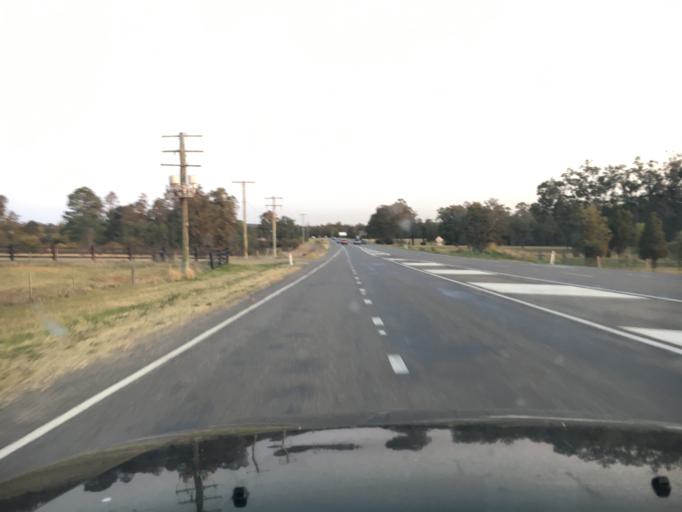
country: AU
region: New South Wales
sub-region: Cessnock
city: Greta
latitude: -32.6671
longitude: 151.3756
